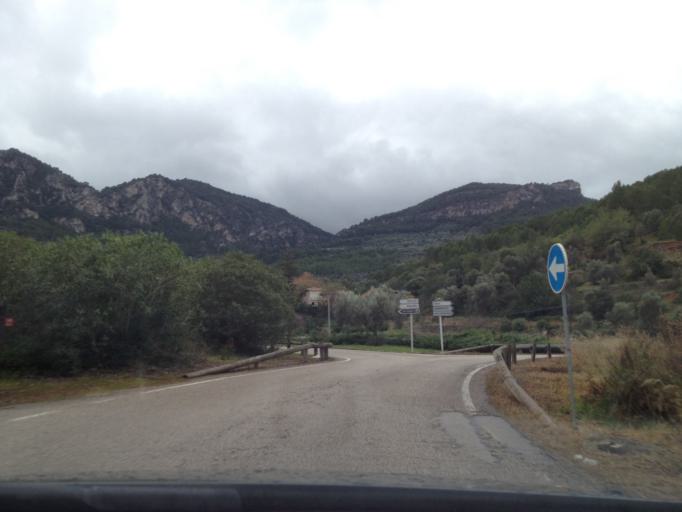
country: ES
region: Balearic Islands
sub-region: Illes Balears
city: Soller
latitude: 39.7723
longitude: 2.7032
